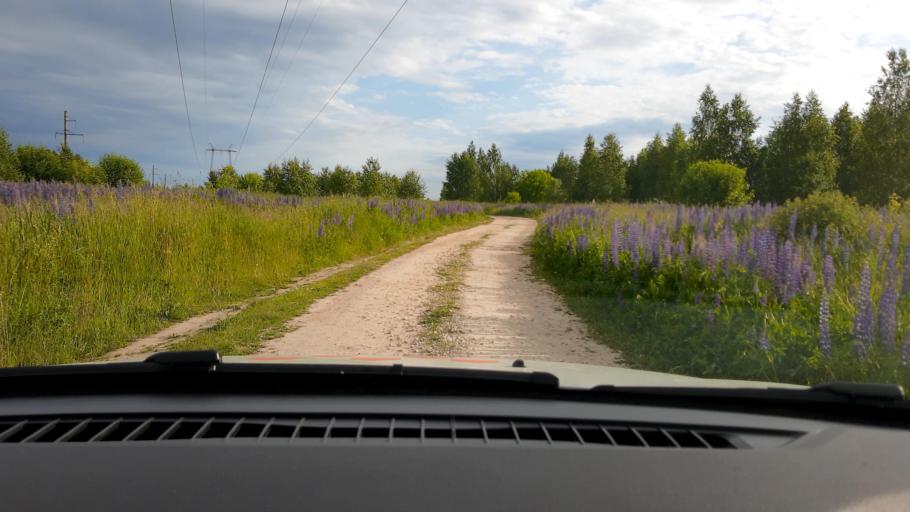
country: RU
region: Nizjnij Novgorod
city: Surovatikha
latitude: 55.8724
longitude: 43.9753
